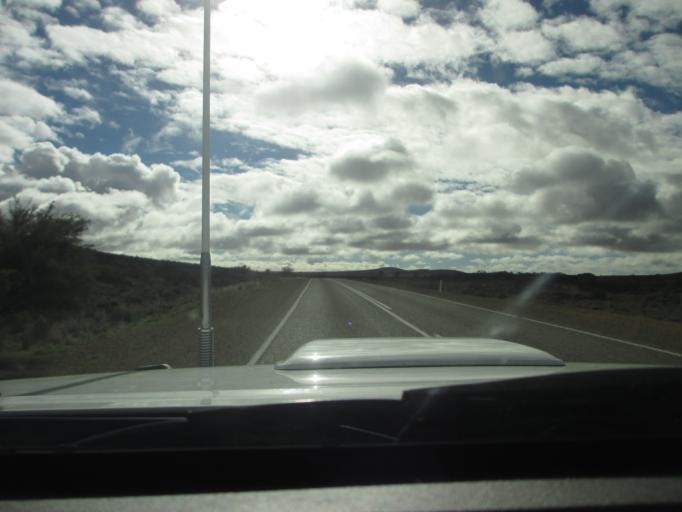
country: AU
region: South Australia
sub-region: Flinders Ranges
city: Quorn
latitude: -32.2040
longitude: 138.5287
